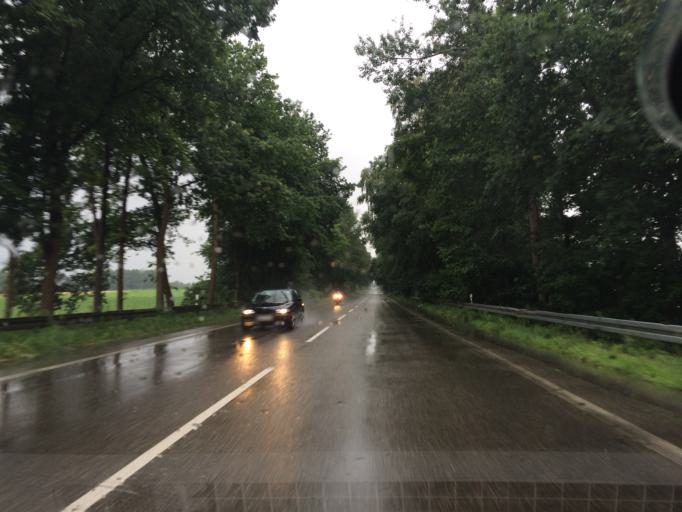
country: DE
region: North Rhine-Westphalia
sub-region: Regierungsbezirk Munster
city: Haltern
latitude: 51.7680
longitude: 7.2009
